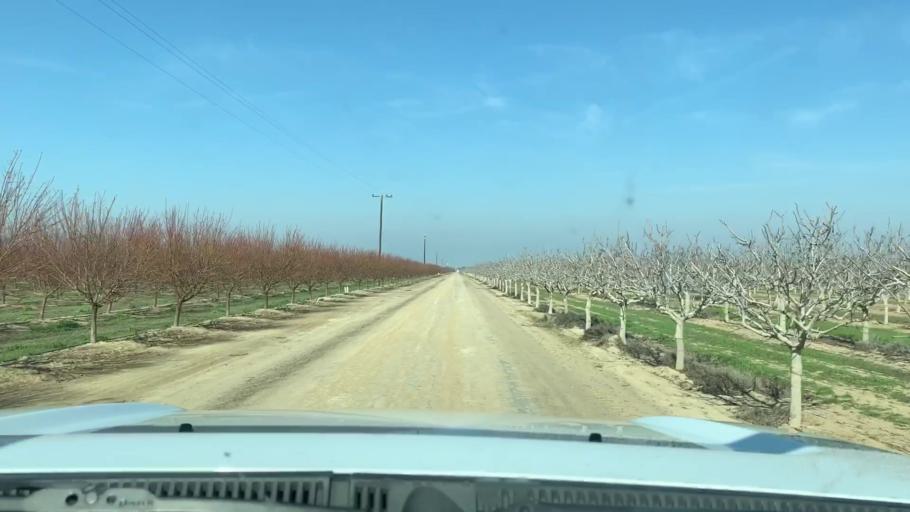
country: US
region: California
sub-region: Kern County
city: Lost Hills
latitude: 35.6053
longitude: -119.5357
